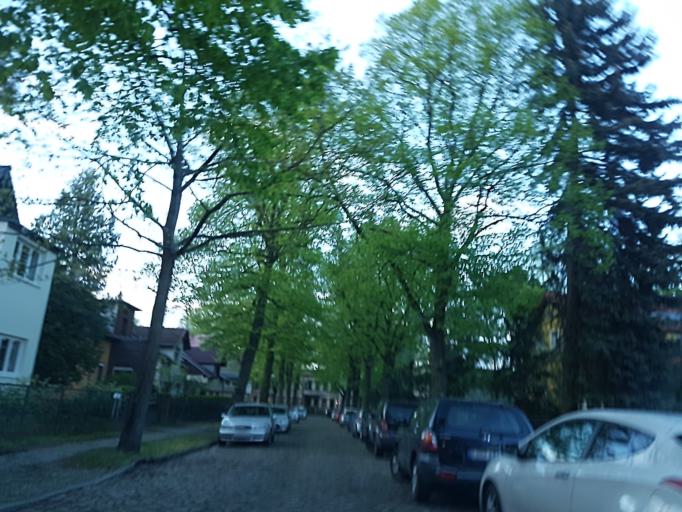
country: DE
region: Berlin
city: Hermsdorf
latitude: 52.6156
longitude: 13.3278
